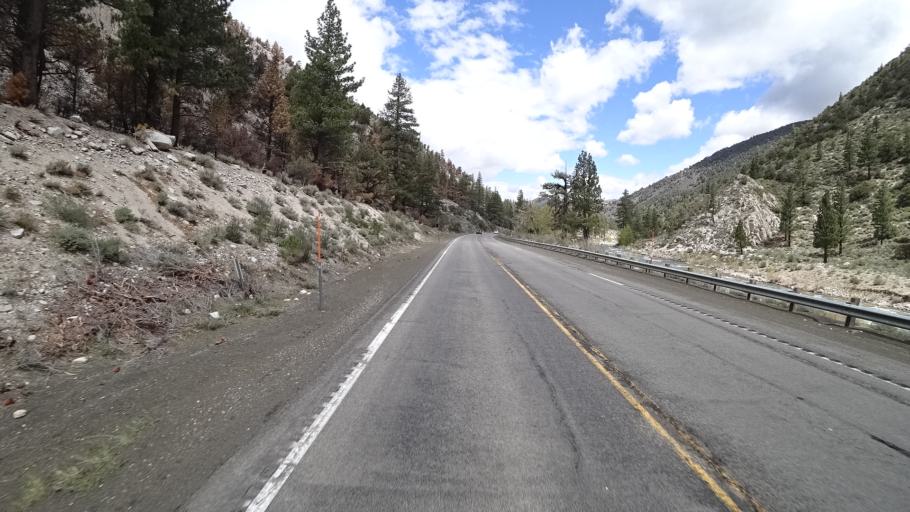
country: US
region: California
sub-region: Mono County
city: Bridgeport
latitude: 38.4130
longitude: -119.4507
